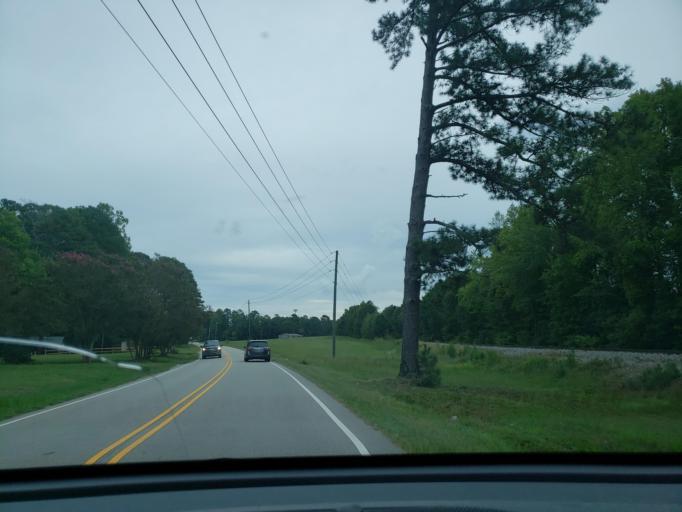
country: US
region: North Carolina
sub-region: Wake County
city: Green Level
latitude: 35.7962
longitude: -78.8644
